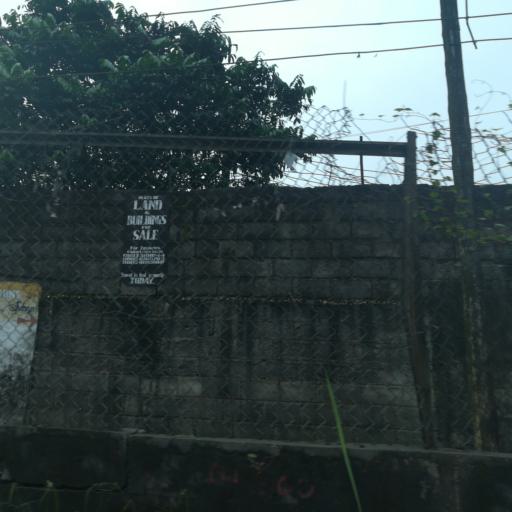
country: NG
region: Rivers
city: Port Harcourt
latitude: 4.7687
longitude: 7.0123
